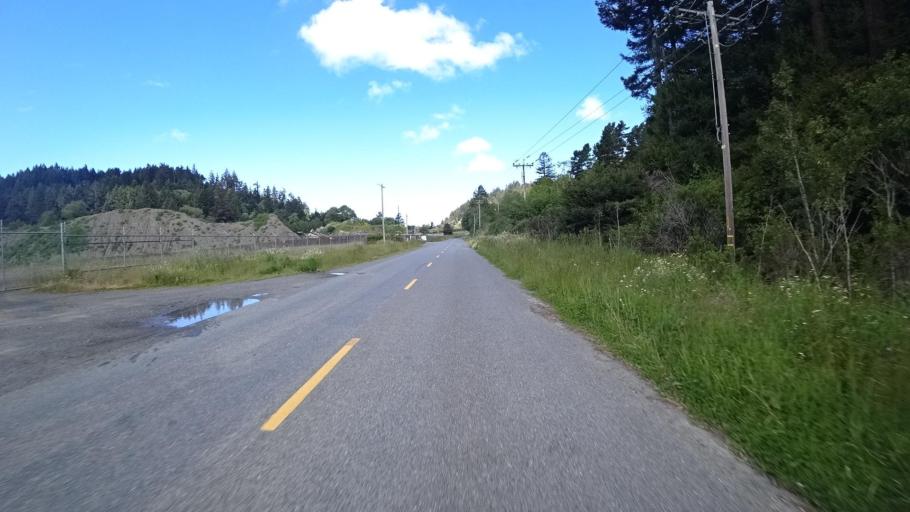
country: US
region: California
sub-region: Humboldt County
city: Arcata
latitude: 40.9066
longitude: -124.0424
